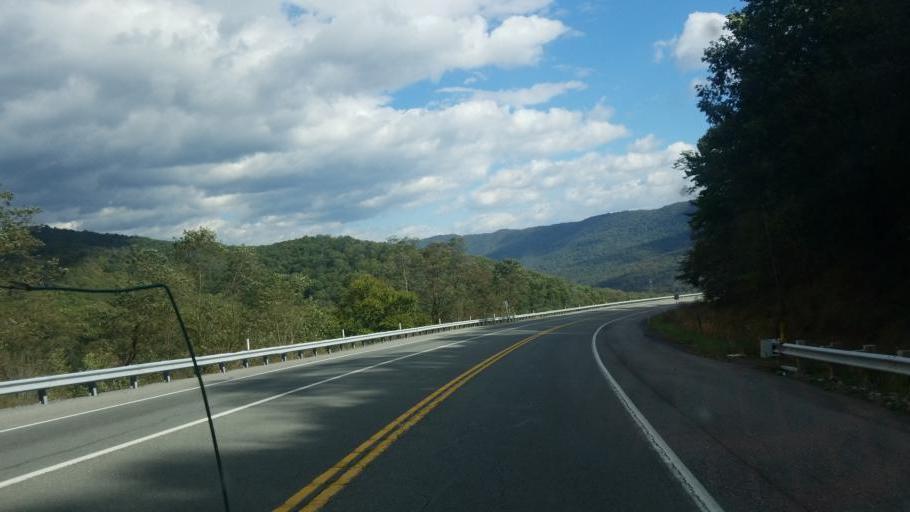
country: US
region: Pennsylvania
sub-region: Fulton County
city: McConnellsburg
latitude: 39.9360
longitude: -77.9282
